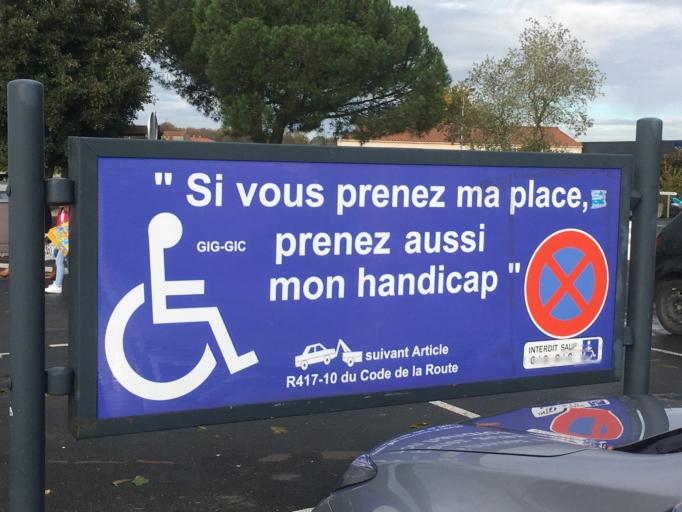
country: FR
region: Pays de la Loire
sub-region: Departement de la Loire-Atlantique
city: Clisson
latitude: 47.0979
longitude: -1.2810
